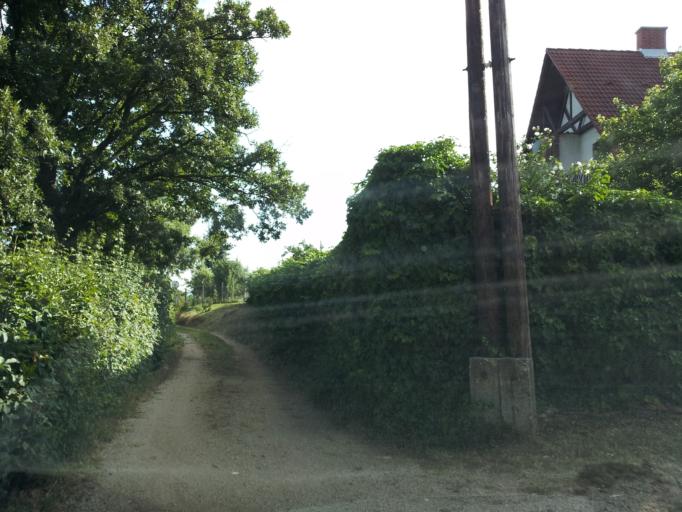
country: HU
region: Veszprem
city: Balatonalmadi
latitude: 47.0031
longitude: 17.9962
